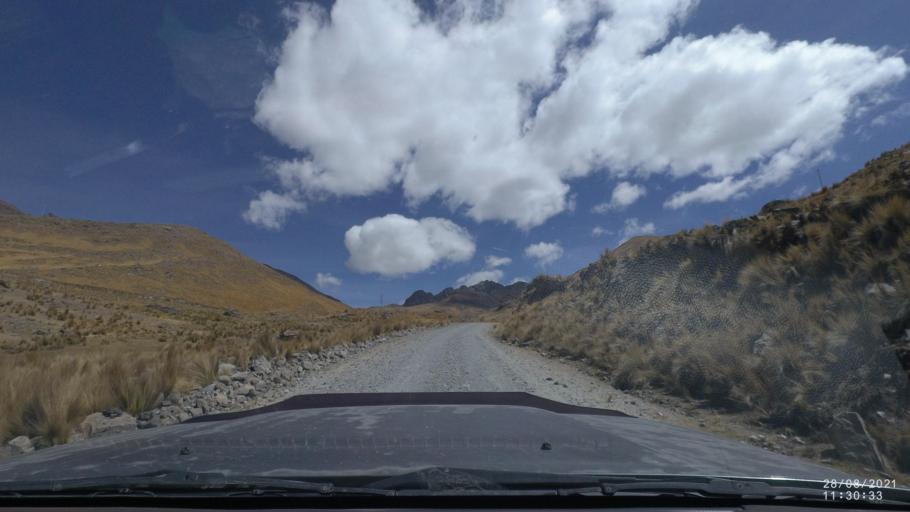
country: BO
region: Cochabamba
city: Sipe Sipe
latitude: -17.1808
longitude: -66.3636
